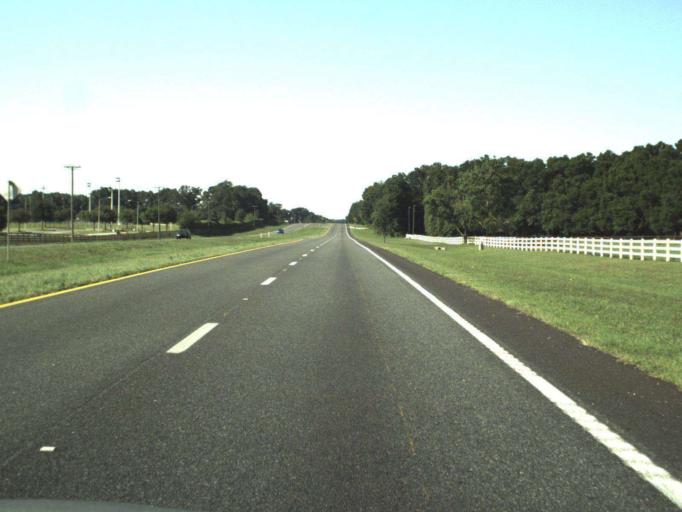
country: US
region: Florida
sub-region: Marion County
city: Citra
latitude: 29.3737
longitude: -82.1328
